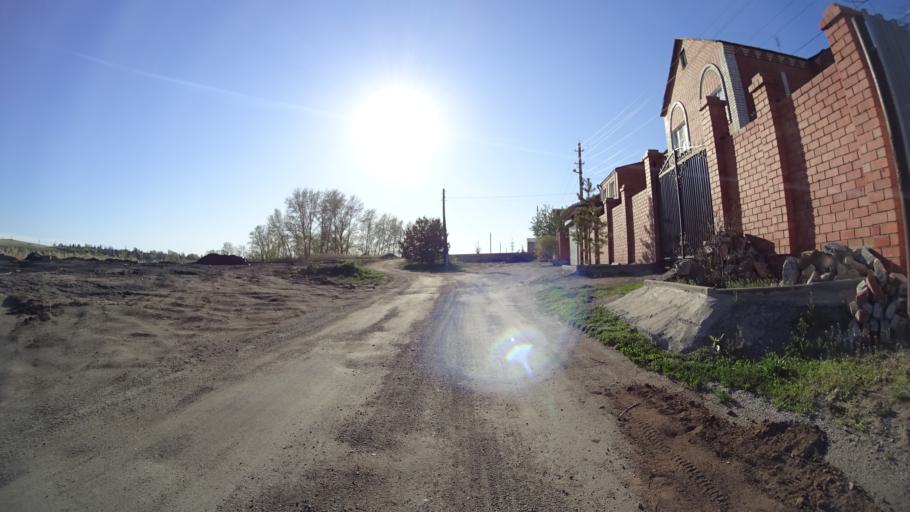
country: RU
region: Chelyabinsk
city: Troitsk
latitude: 54.0683
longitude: 61.5363
